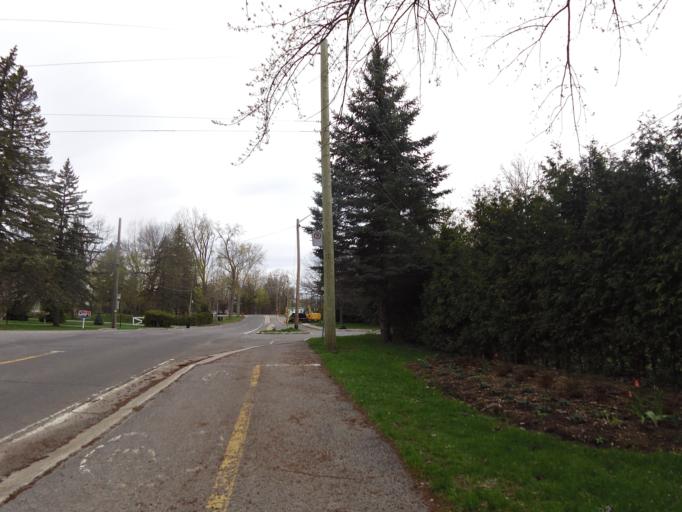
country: CA
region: Quebec
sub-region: Laurentides
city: Deux-Montagnes
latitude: 45.5300
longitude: -73.8799
